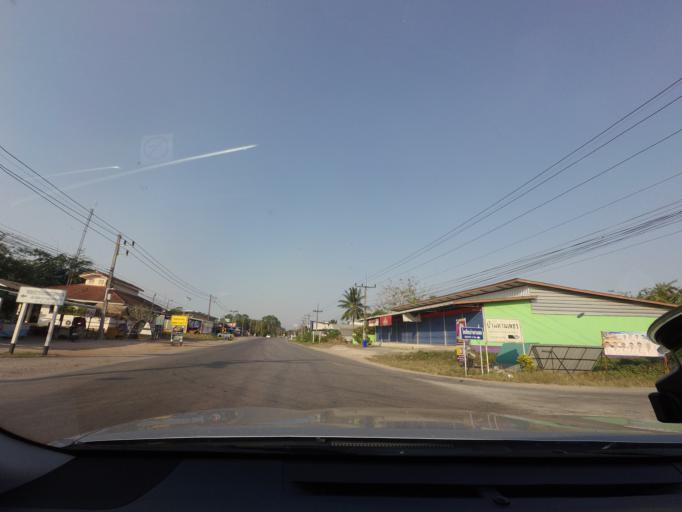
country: TH
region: Surat Thani
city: Phrasaeng
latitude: 8.5805
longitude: 99.2794
